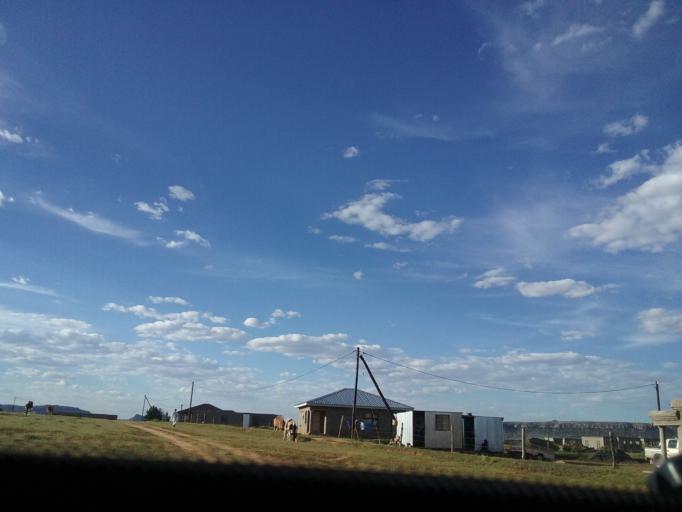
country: LS
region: Maseru
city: Maseru
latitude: -29.4280
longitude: 27.5697
